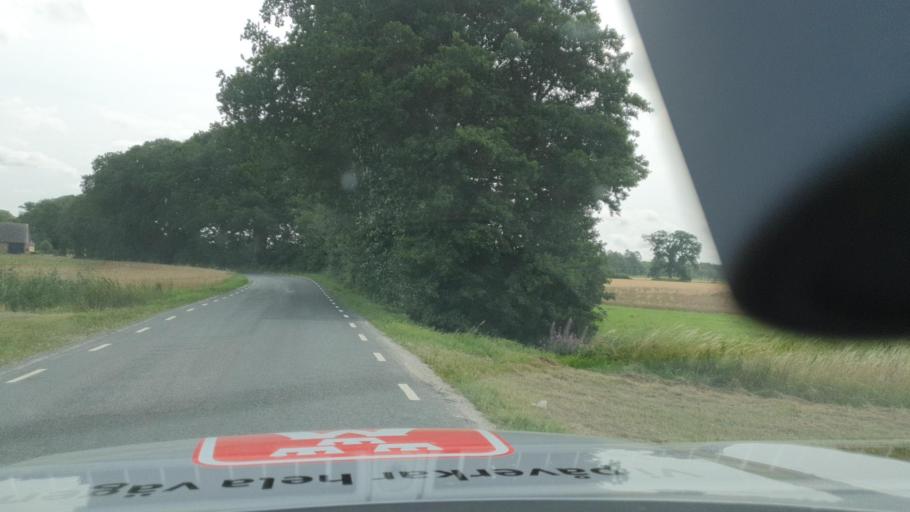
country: SE
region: Skane
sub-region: Kristianstads Kommun
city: Fjalkinge
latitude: 56.0543
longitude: 14.3766
